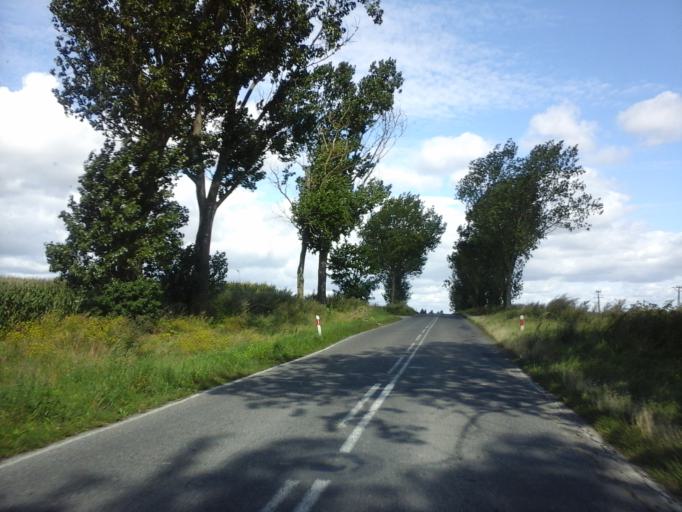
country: PL
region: West Pomeranian Voivodeship
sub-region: Powiat stargardzki
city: Stargard Szczecinski
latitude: 53.2718
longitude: 15.0865
